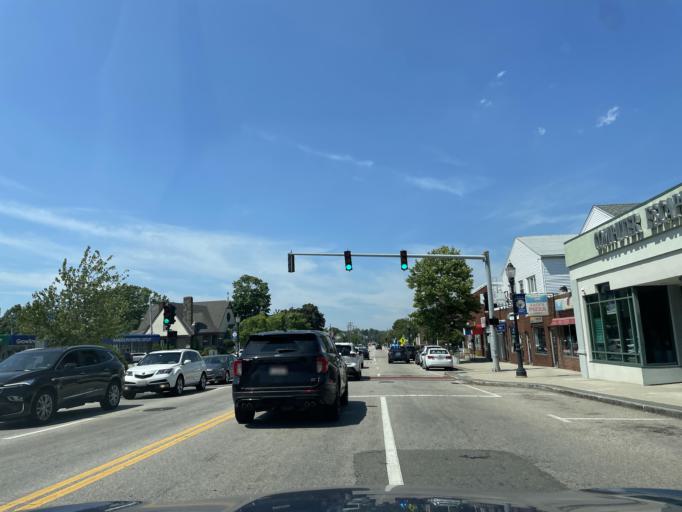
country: US
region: Massachusetts
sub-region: Norfolk County
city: Randolph
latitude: 42.1639
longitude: -71.0422
